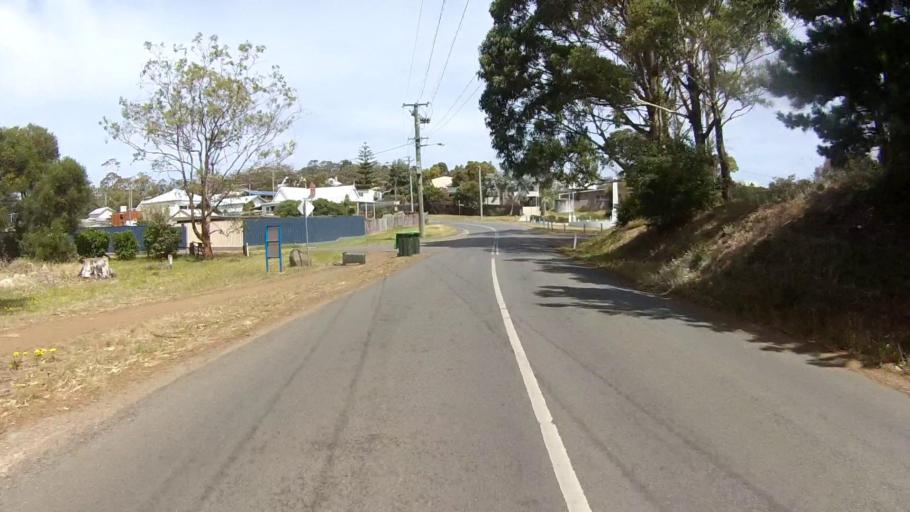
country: AU
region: Tasmania
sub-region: Kingborough
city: Blackmans Bay
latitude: -43.0267
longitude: 147.4169
